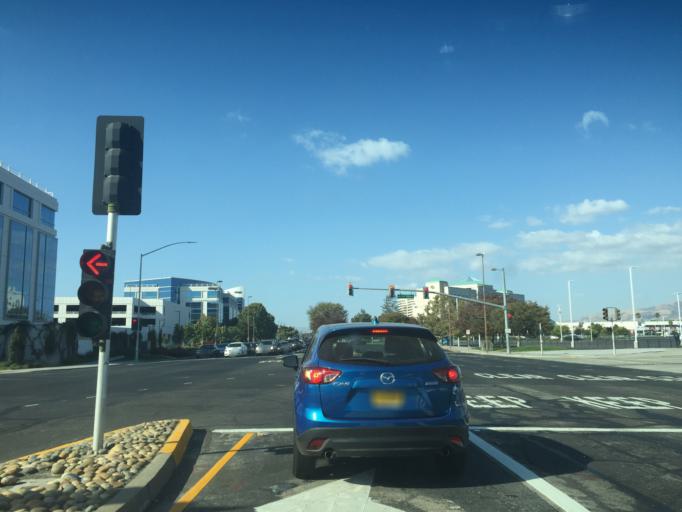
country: US
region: California
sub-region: Santa Clara County
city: Santa Clara
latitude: 37.3995
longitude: -121.9779
